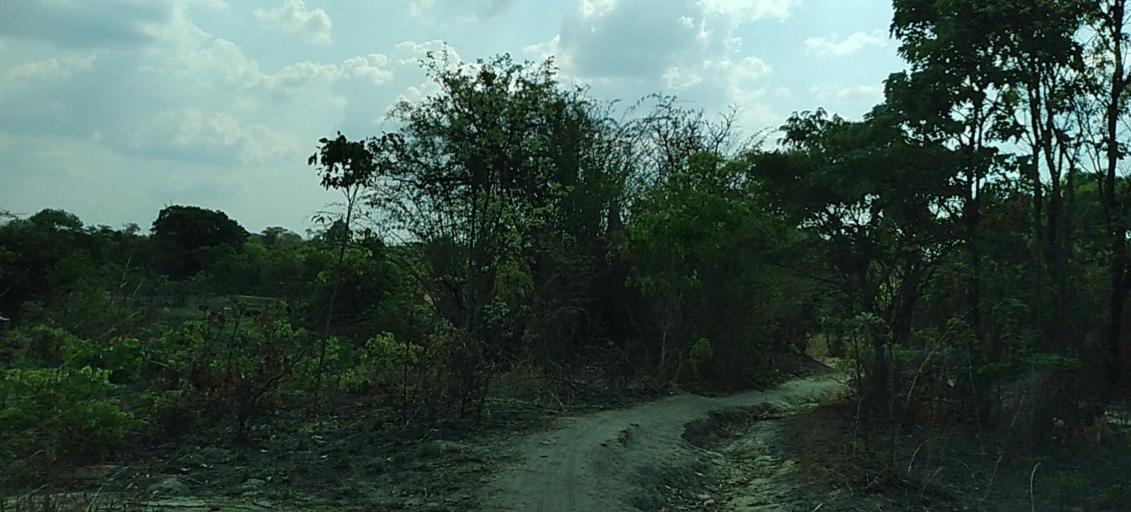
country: ZM
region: Copperbelt
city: Luanshya
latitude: -13.2265
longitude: 28.3328
